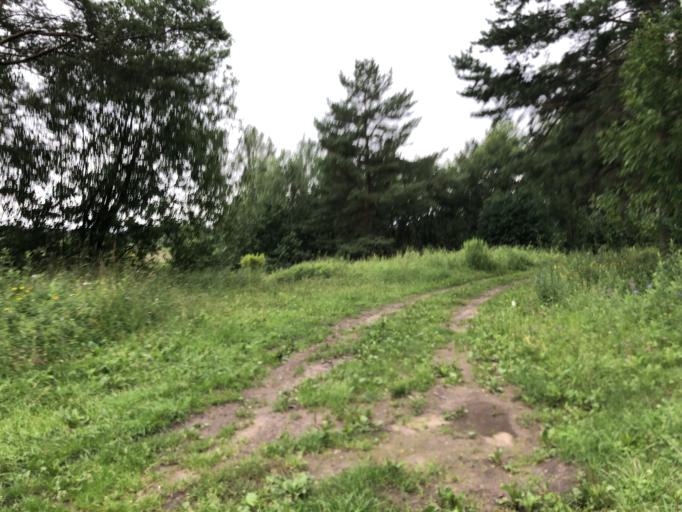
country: RU
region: Tverskaya
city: Rzhev
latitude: 56.2472
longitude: 34.3688
